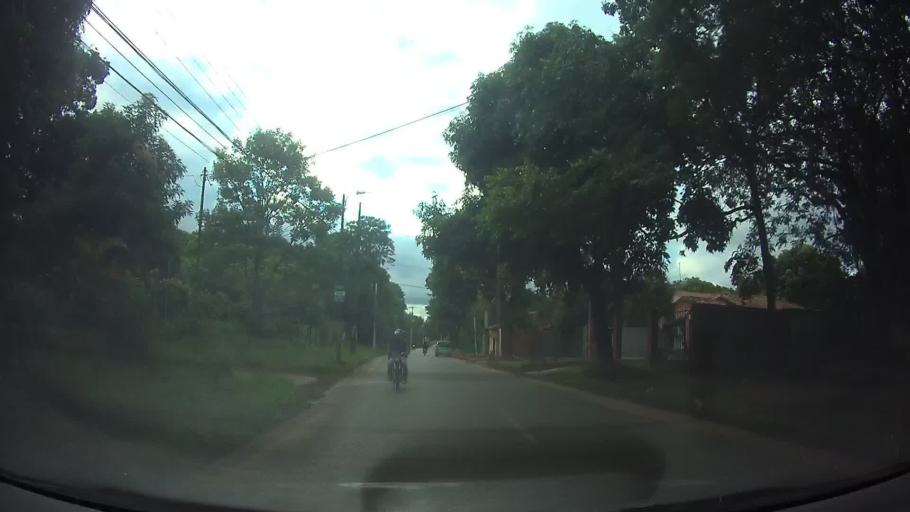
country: PY
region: Central
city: San Lorenzo
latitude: -25.3038
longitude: -57.4949
